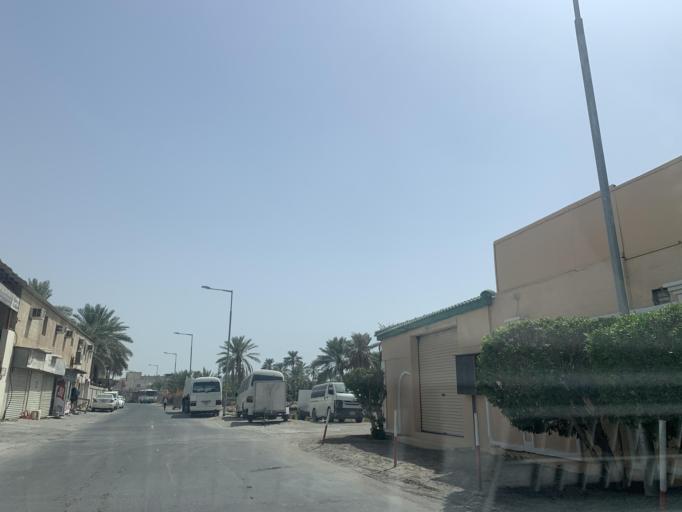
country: BH
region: Central Governorate
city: Madinat Hamad
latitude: 26.1480
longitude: 50.4952
